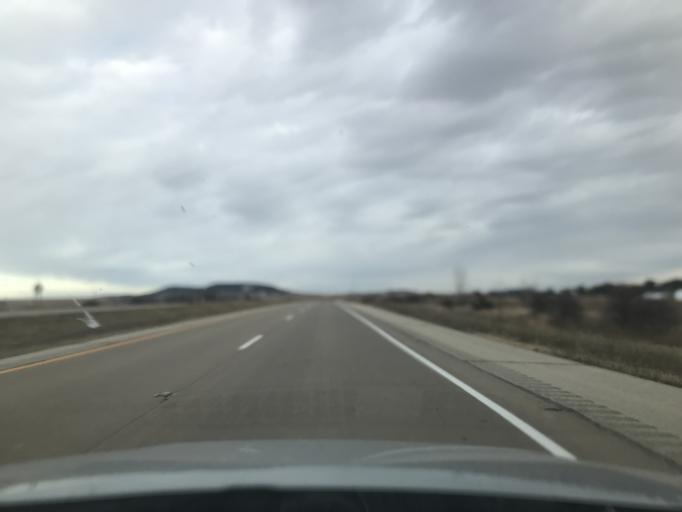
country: US
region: Wisconsin
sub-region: Grant County
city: Platteville
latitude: 42.7312
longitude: -90.4354
